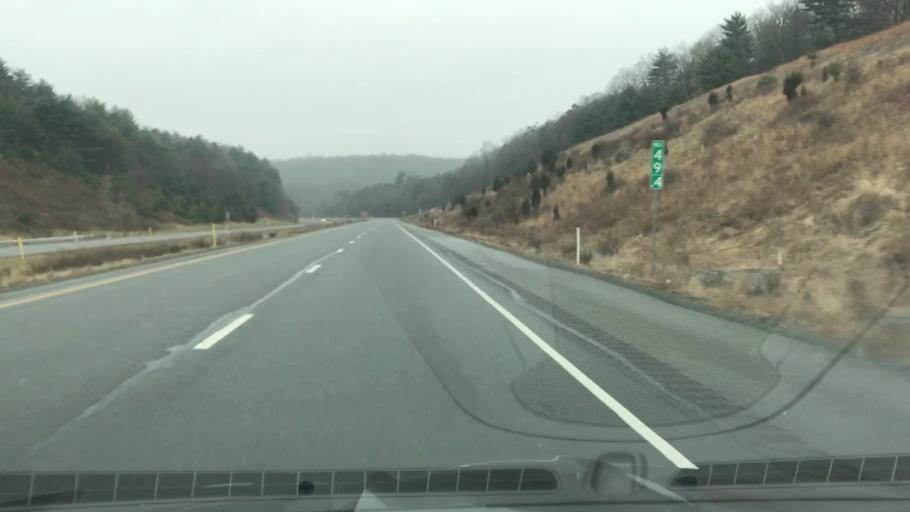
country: US
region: Pennsylvania
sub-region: Pike County
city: Milford
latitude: 41.3424
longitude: -74.7822
